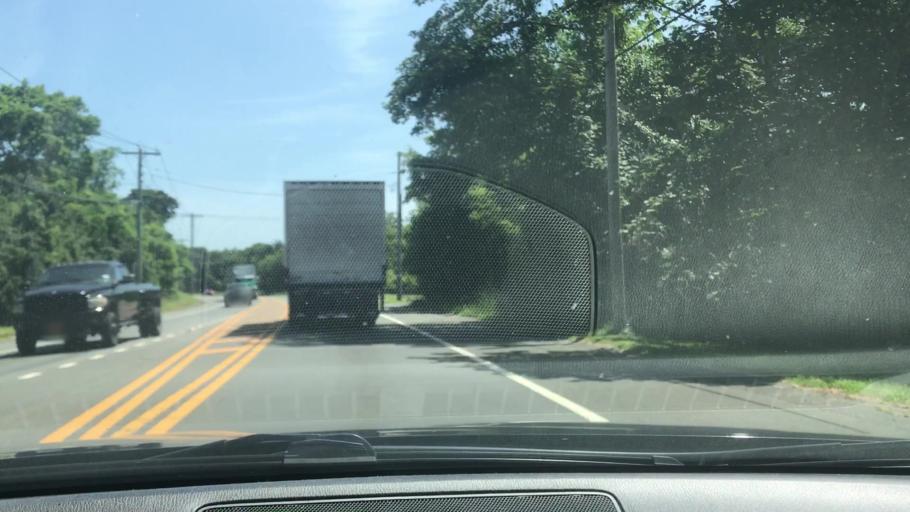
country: US
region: New York
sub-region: Suffolk County
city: Bridgehampton
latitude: 40.9410
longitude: -72.2783
